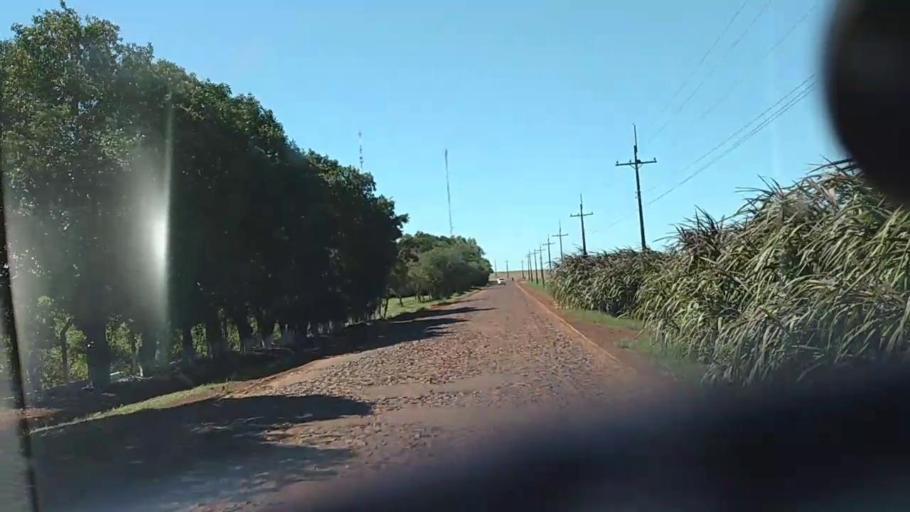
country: PY
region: Alto Parana
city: Naranjal
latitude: -25.9767
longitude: -55.1653
